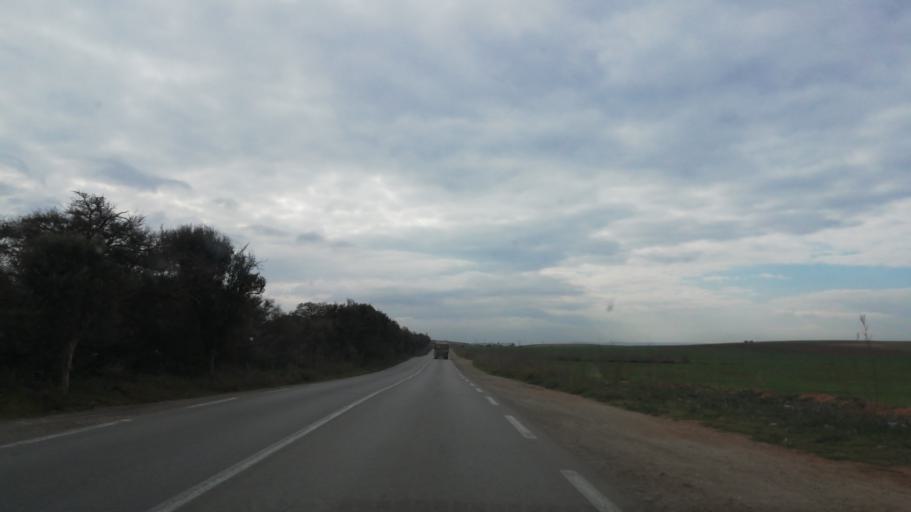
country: DZ
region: Oran
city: Ain el Bya
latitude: 35.7627
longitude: -0.3494
